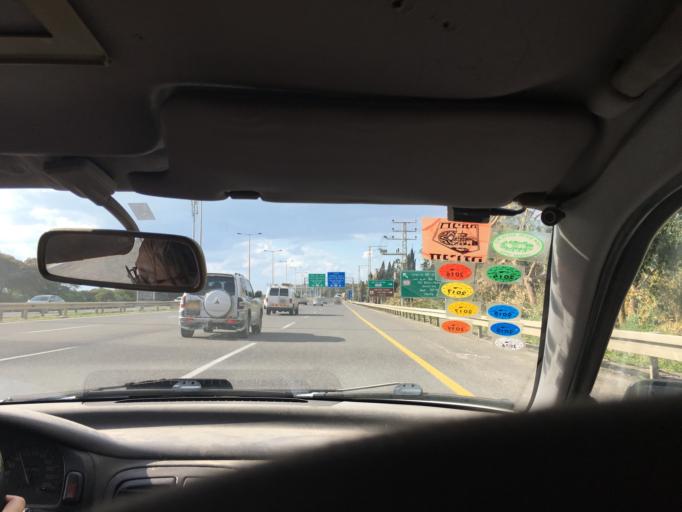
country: IL
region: Tel Aviv
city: Ramat HaSharon
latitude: 32.1376
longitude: 34.8263
